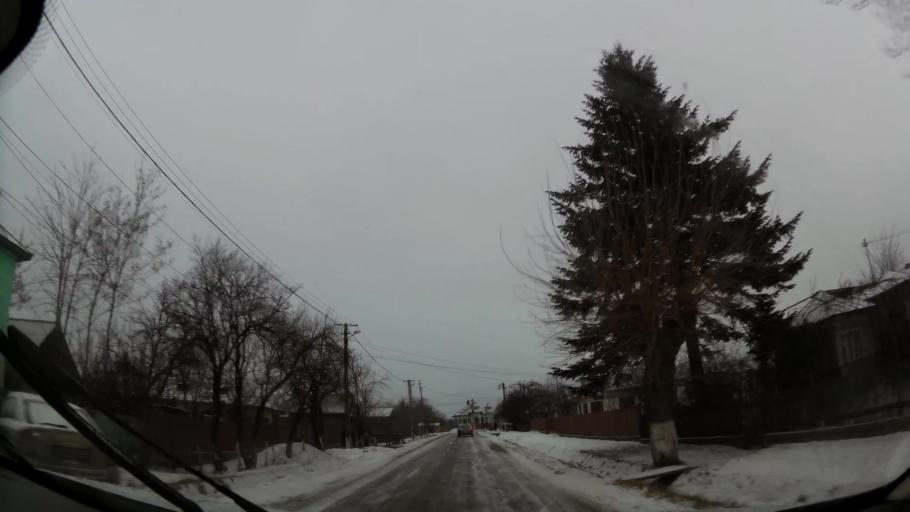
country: RO
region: Prahova
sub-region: Comuna Poenarii-Burchi
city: Ologeni
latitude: 44.7335
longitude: 25.9478
